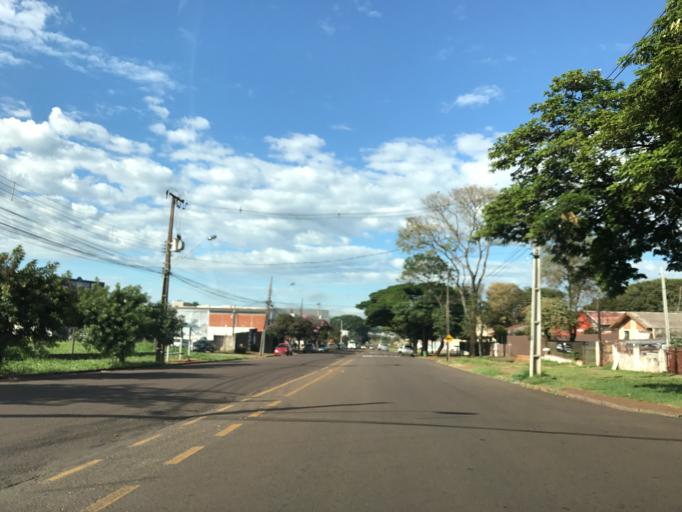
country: BR
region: Parana
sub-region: Maringa
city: Maringa
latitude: -23.4509
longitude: -51.9539
